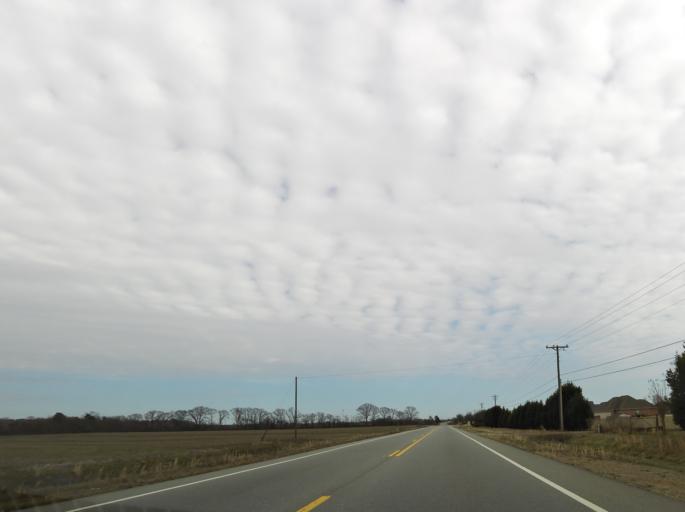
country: US
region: Georgia
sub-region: Peach County
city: Byron
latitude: 32.6065
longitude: -83.7728
